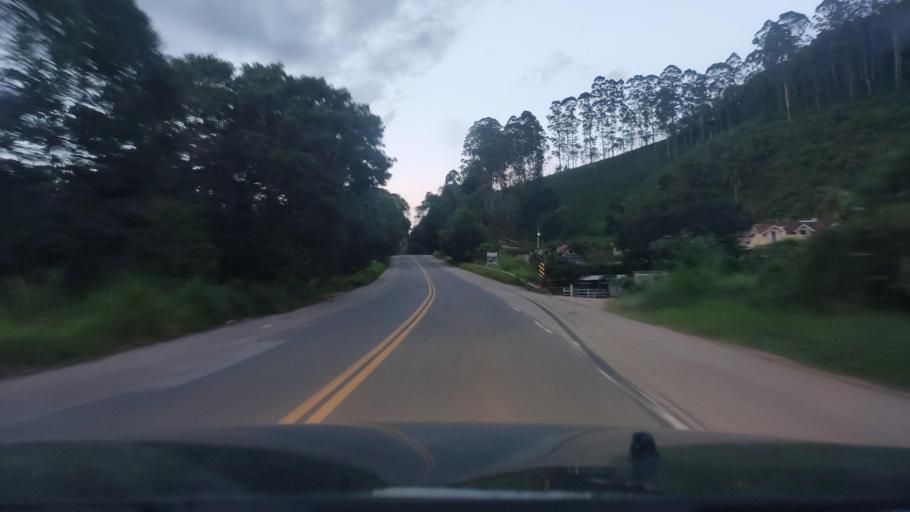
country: BR
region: Sao Paulo
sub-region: Campos Do Jordao
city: Campos do Jordao
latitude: -22.7645
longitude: -45.7399
